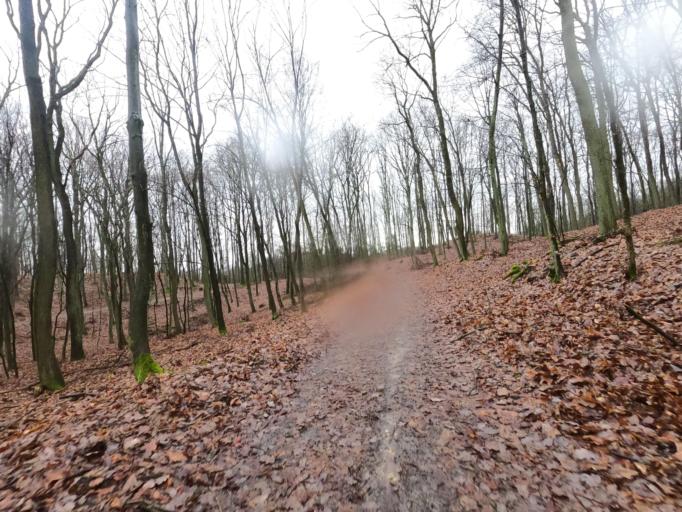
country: PL
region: Greater Poland Voivodeship
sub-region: Powiat pilski
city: Wyrzysk
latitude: 53.1282
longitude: 17.2489
